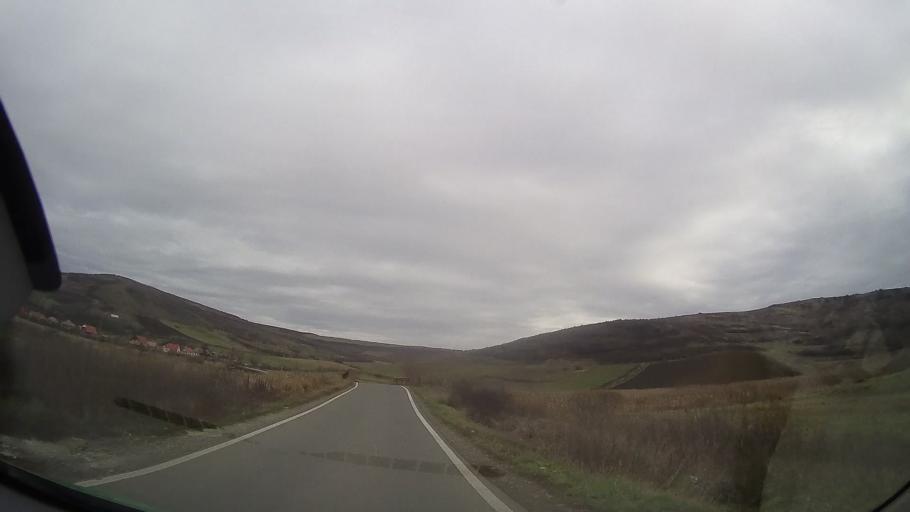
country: RO
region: Mures
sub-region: Comuna Faragau
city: Faragau
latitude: 46.7731
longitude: 24.5575
